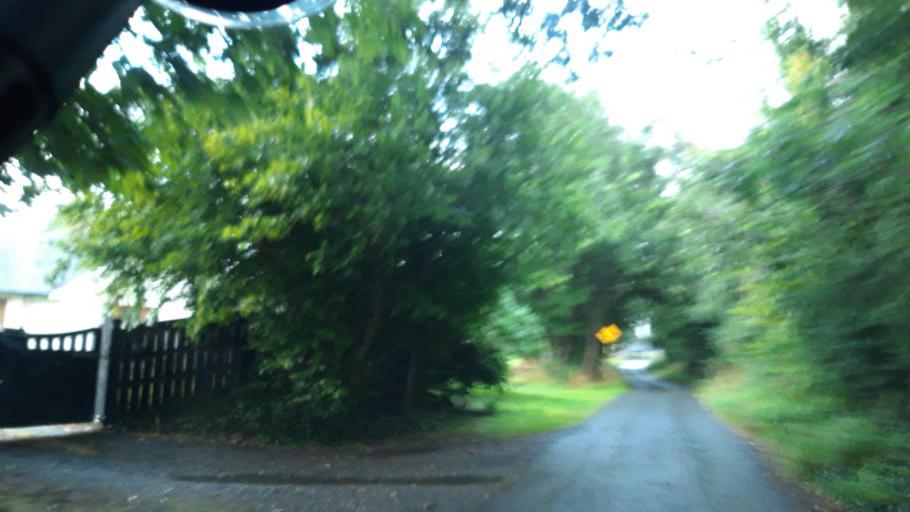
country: IE
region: Leinster
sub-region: Kildare
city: Leixlip
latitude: 53.3376
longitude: -6.4968
